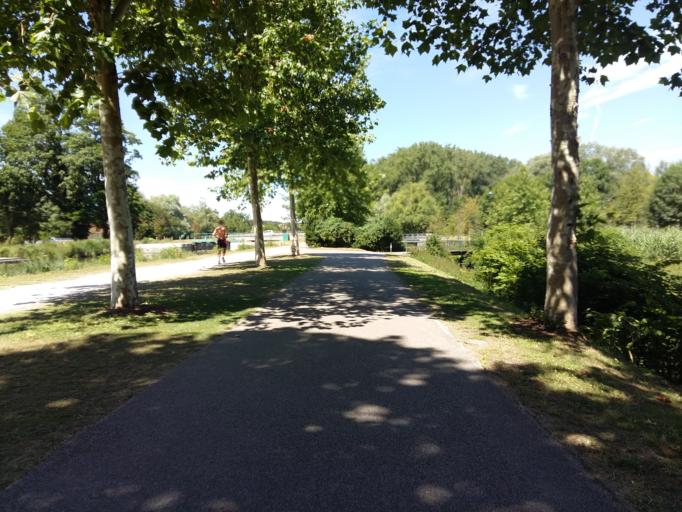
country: FR
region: Picardie
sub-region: Departement de la Somme
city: Dreuil-les-Amiens
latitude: 49.9182
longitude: 2.2592
